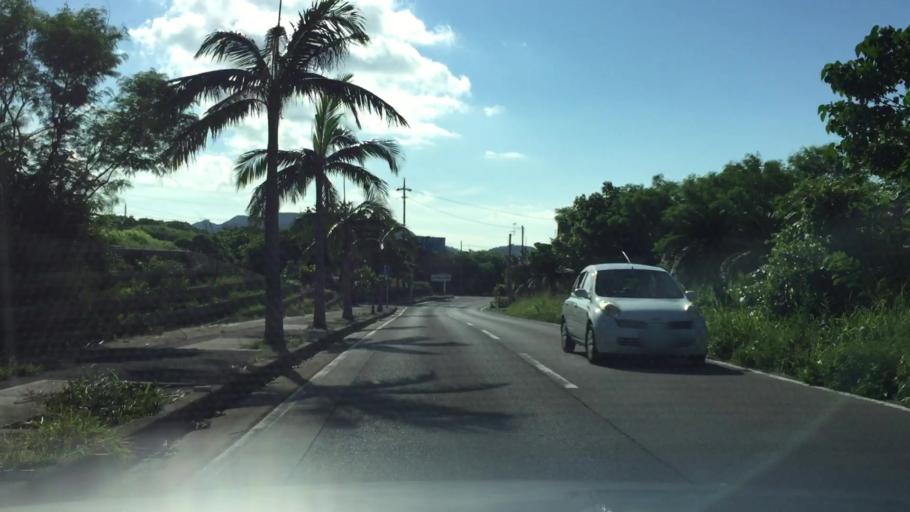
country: JP
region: Okinawa
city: Ishigaki
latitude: 24.4477
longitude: 124.1691
